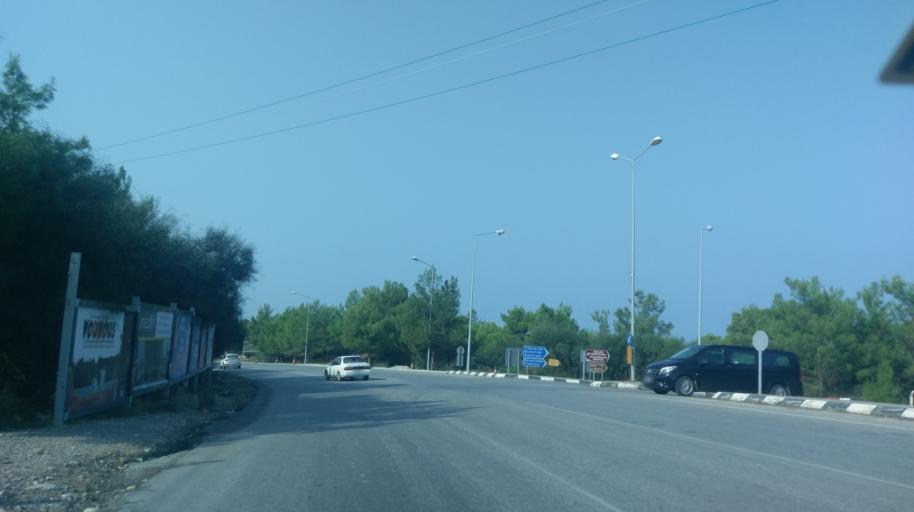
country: CY
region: Keryneia
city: Kyrenia
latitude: 35.3264
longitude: 33.4144
